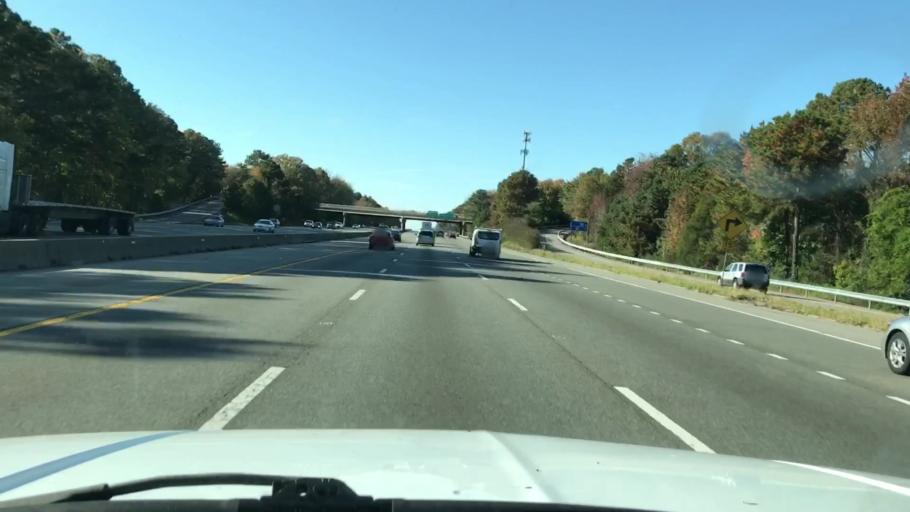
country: US
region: Virginia
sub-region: Henrico County
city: Tuckahoe
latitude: 37.6227
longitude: -77.5505
